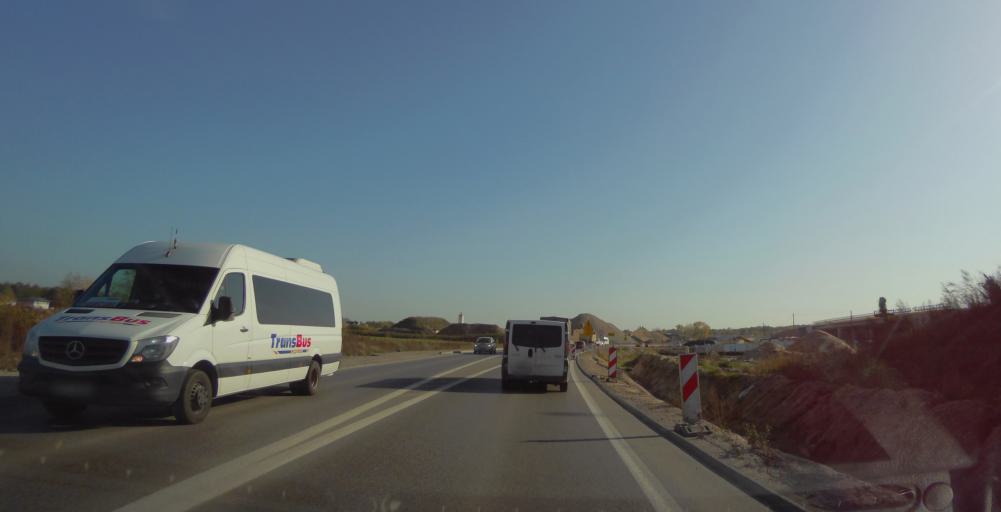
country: PL
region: Masovian Voivodeship
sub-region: Powiat minski
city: Sulejowek
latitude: 52.1867
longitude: 21.2847
